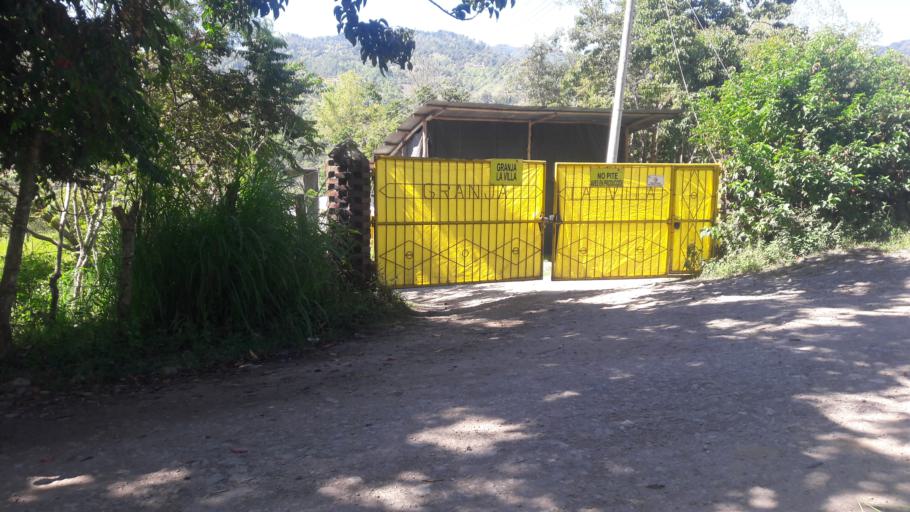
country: CO
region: Cundinamarca
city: Tenza
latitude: 5.0882
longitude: -73.4241
